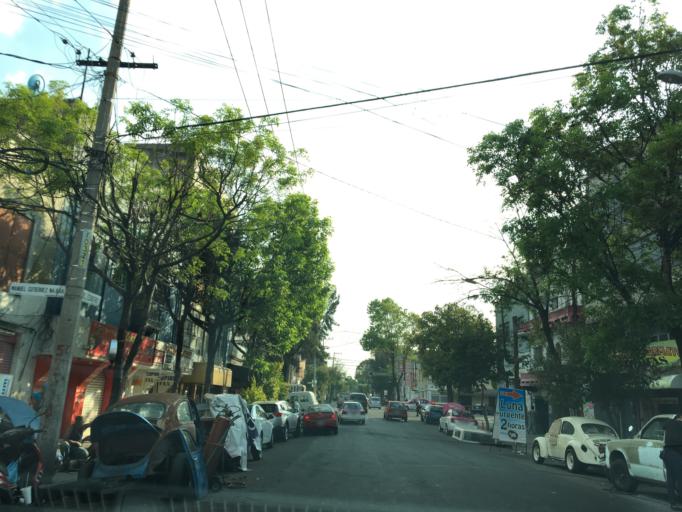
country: MX
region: Mexico City
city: Mexico City
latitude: 19.4153
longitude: -99.1366
